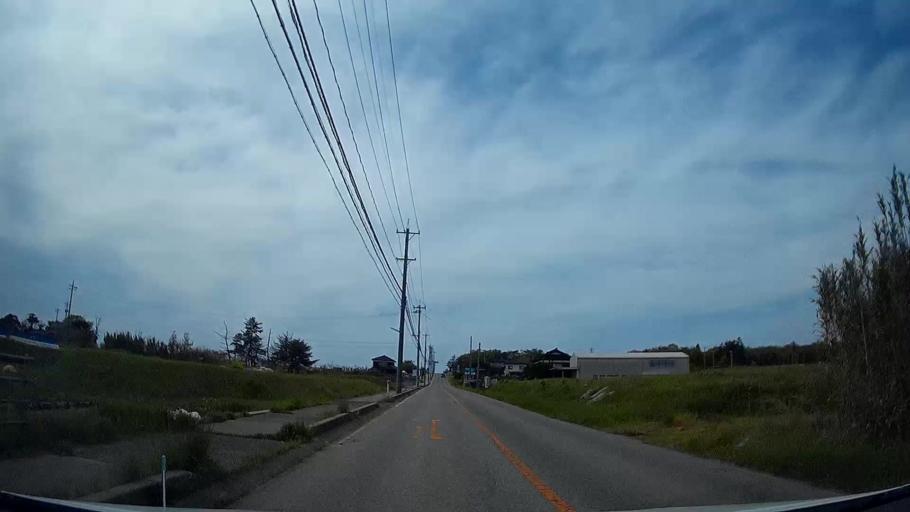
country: JP
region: Ishikawa
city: Hakui
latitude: 37.0148
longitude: 136.7544
